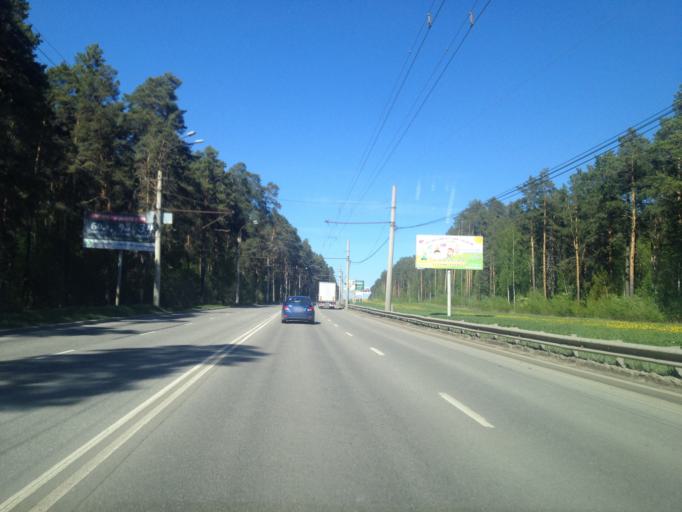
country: RU
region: Sverdlovsk
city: Sovkhoznyy
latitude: 56.7810
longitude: 60.5600
